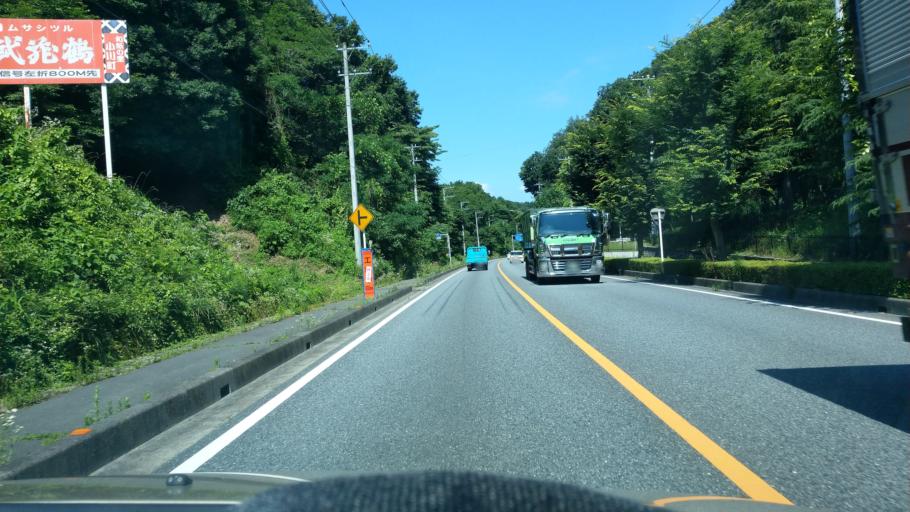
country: JP
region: Saitama
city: Ogawa
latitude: 36.0682
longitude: 139.2570
